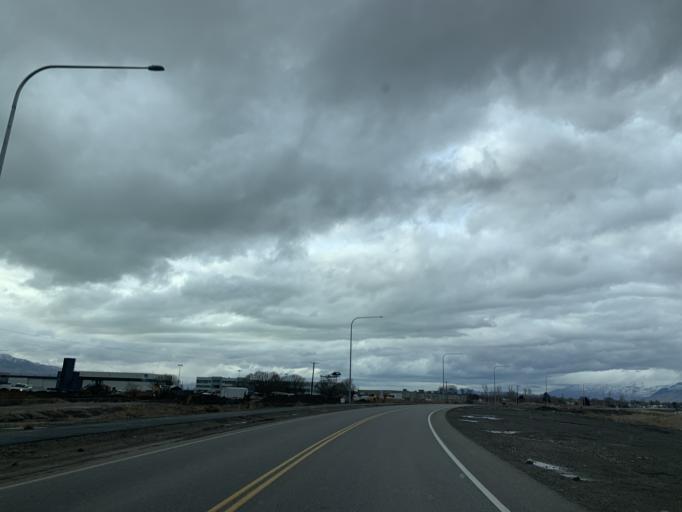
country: US
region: Utah
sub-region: Utah County
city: Provo
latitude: 40.2162
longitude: -111.7118
